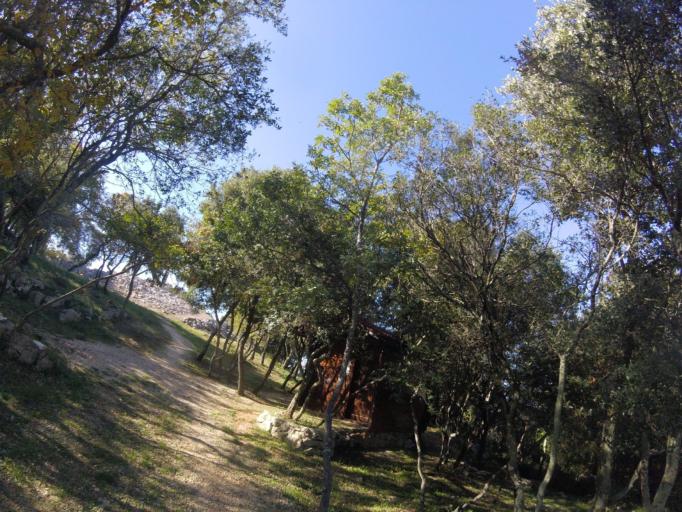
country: HR
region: Istarska
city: Vrsar
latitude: 45.1406
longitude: 13.6538
